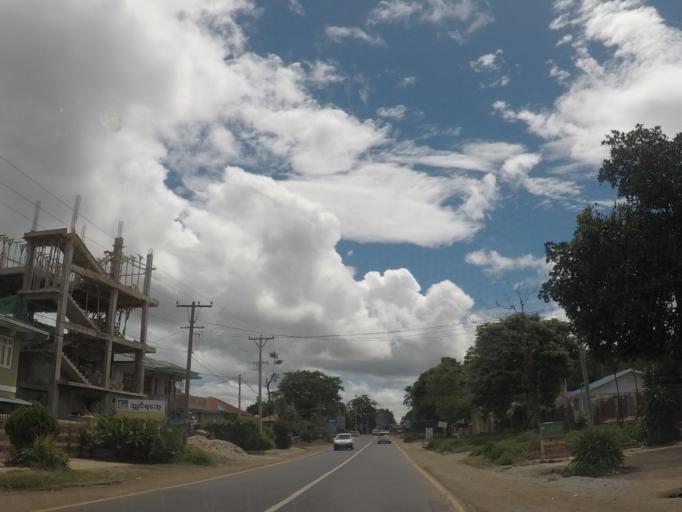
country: MM
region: Mandalay
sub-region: Pyin Oo Lwin District
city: Pyin Oo Lwin
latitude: 22.0608
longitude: 96.5209
